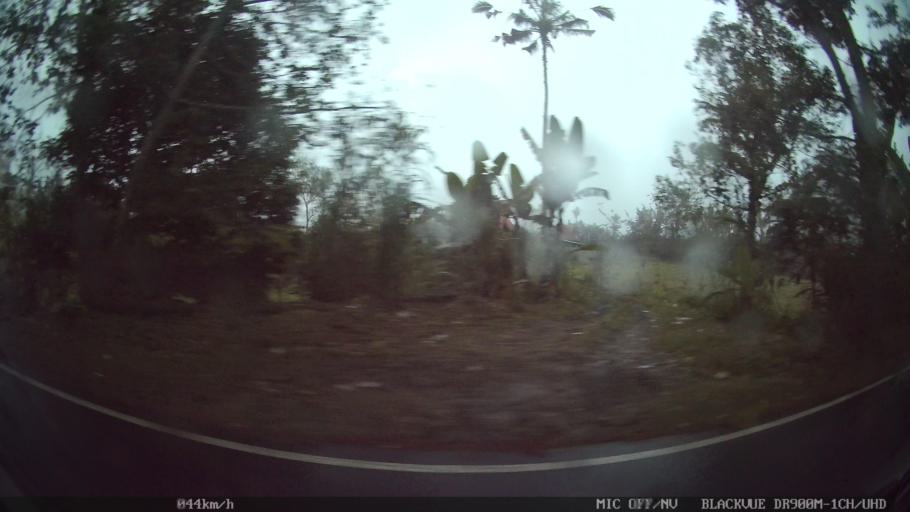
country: ID
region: Bali
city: Banjar Taro Kelod
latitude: -8.3277
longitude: 115.2917
